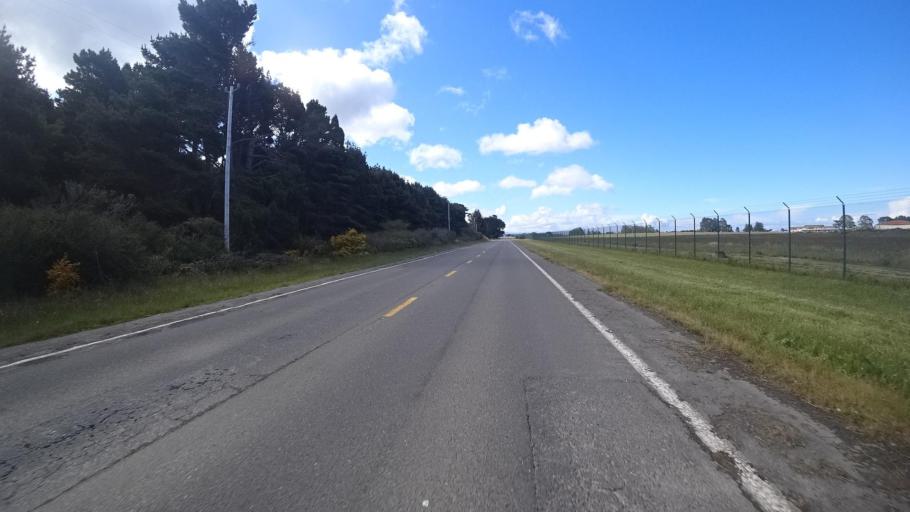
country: US
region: California
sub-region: Humboldt County
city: McKinleyville
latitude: 40.9756
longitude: -124.1006
